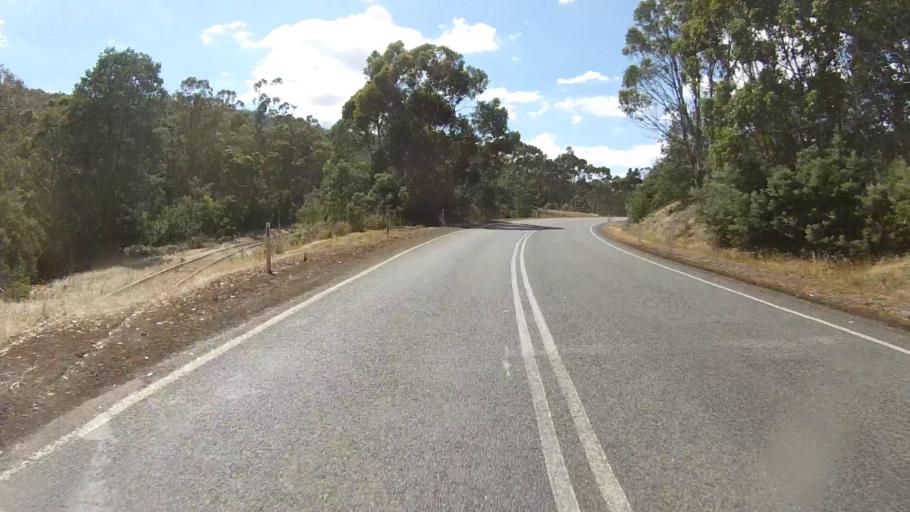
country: AU
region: Tasmania
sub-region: Derwent Valley
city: New Norfolk
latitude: -42.6820
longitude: 146.7365
